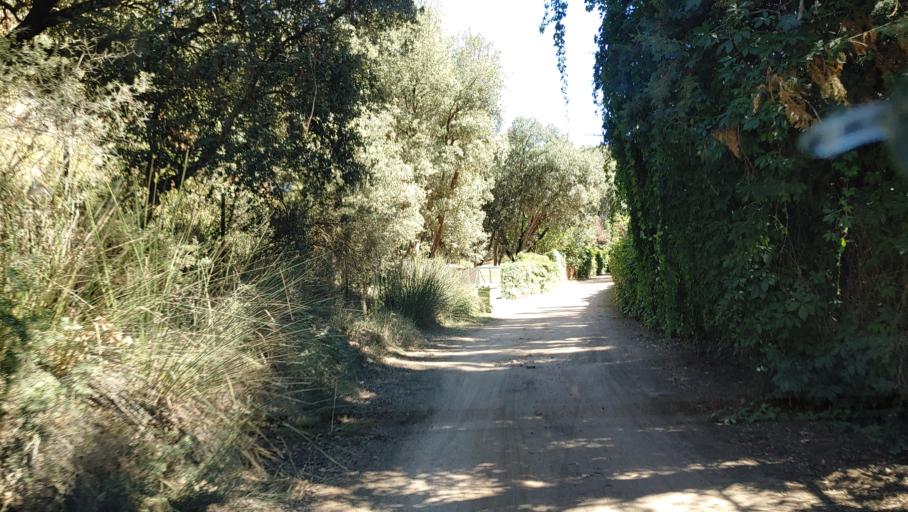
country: ES
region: Castille-La Mancha
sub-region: Provincia de Albacete
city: Ossa de Montiel
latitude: 38.9245
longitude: -2.8111
